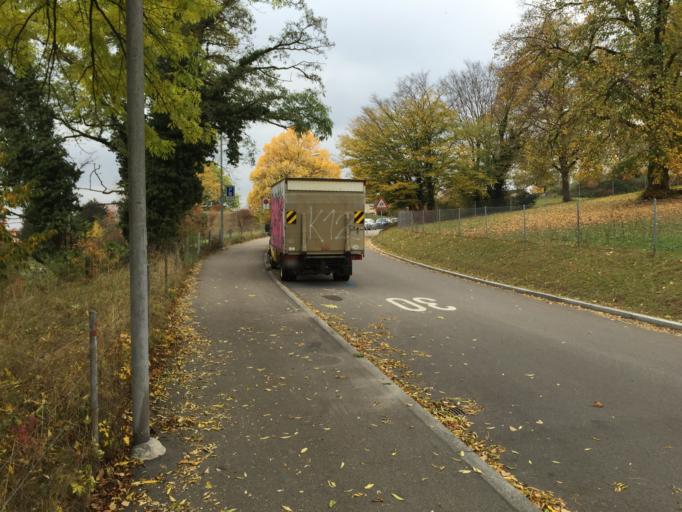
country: CH
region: Zurich
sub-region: Bezirk Zuerich
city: Zuerich (Kreis 11) / Seebach
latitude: 47.4196
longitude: 8.5422
